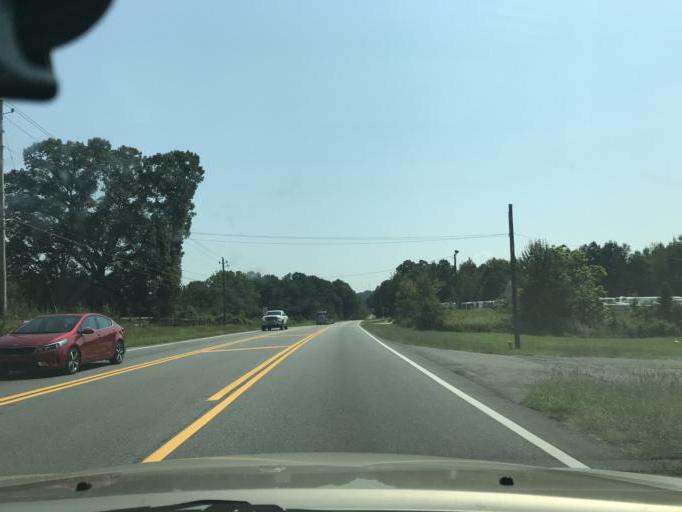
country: US
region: Georgia
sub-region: Hall County
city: Flowery Branch
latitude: 34.2472
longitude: -84.0185
